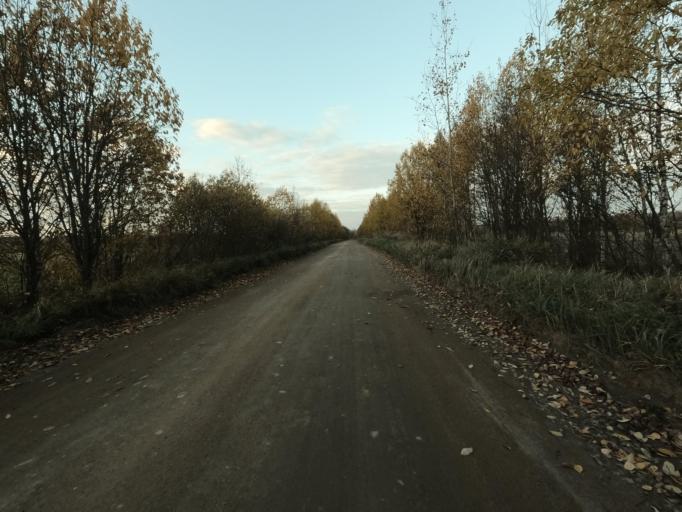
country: RU
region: Leningrad
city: Mga
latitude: 59.8017
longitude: 31.2005
